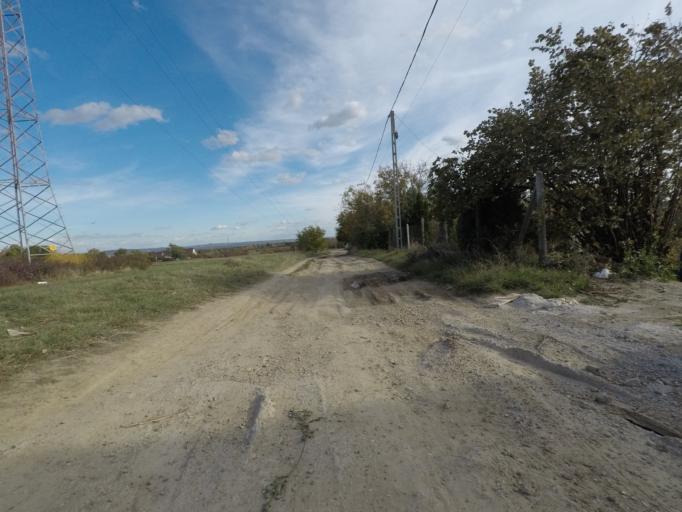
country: HU
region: Pest
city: Pomaz
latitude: 47.6316
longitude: 19.0259
